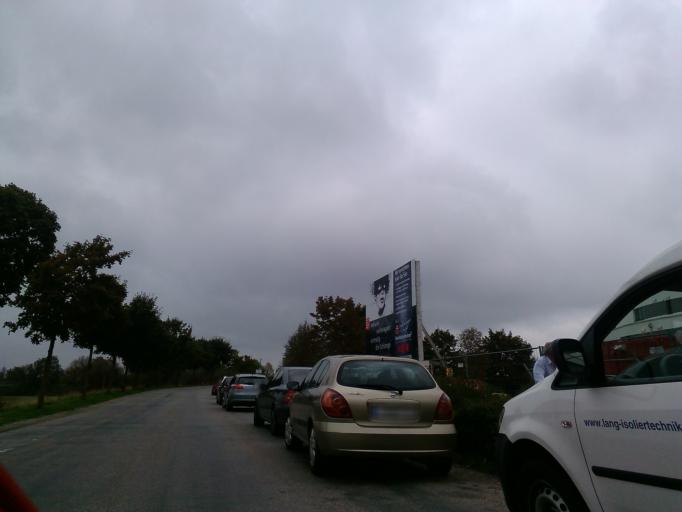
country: DE
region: Bavaria
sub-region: Upper Bavaria
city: Fuerstenfeldbruck
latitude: 48.1832
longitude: 11.2417
